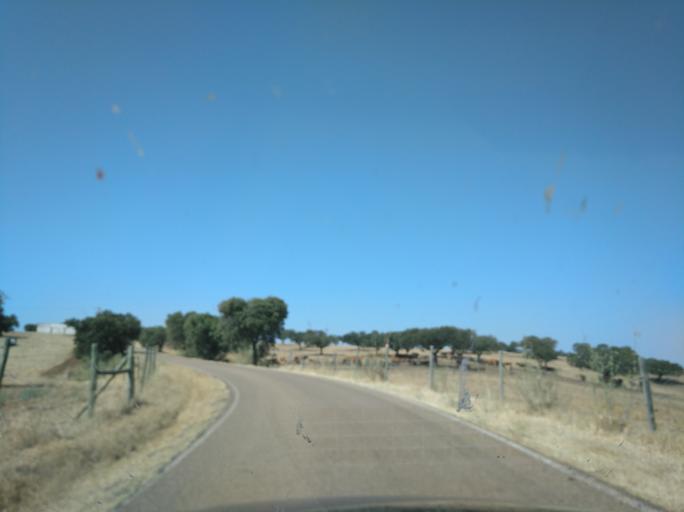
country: PT
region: Portalegre
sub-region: Campo Maior
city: Campo Maior
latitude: 39.0477
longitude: -7.0117
